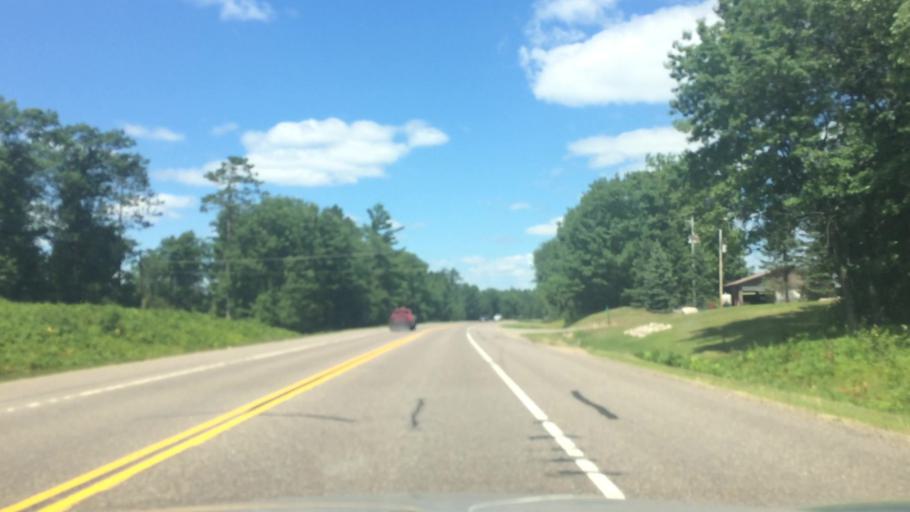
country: US
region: Wisconsin
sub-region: Vilas County
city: Lac du Flambeau
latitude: 45.9460
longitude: -89.6991
